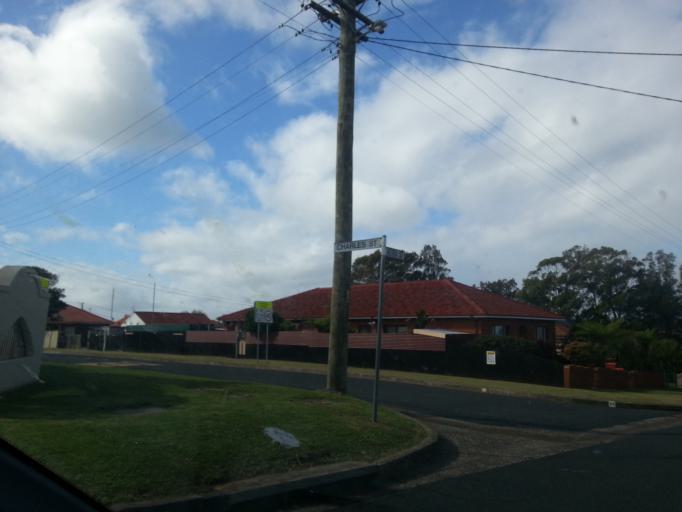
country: AU
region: New South Wales
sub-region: Wollongong
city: Port Kembla
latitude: -34.4851
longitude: 150.9010
